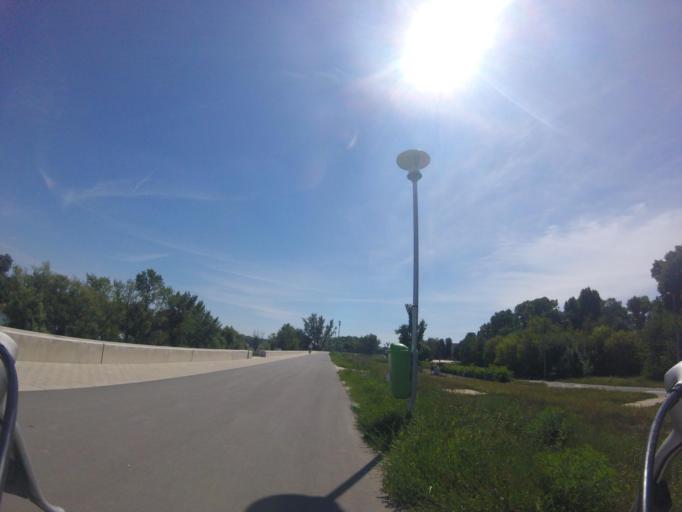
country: HU
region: Pest
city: Budakalasz
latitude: 47.5956
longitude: 19.0699
